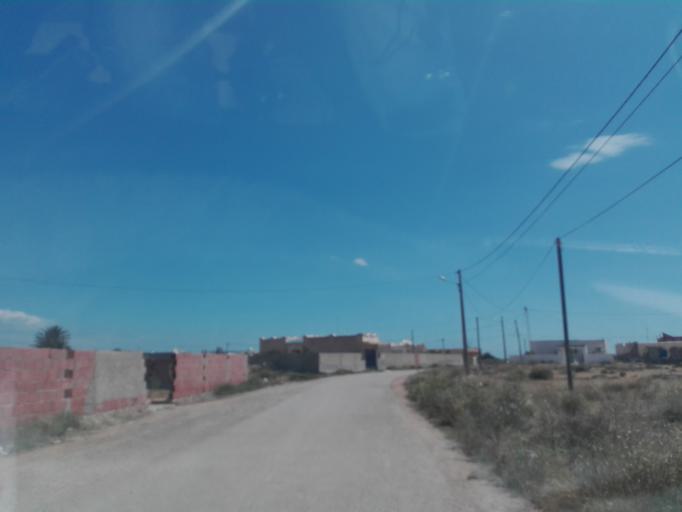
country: TN
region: Safaqis
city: Jabinyanah
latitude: 34.8162
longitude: 11.2616
